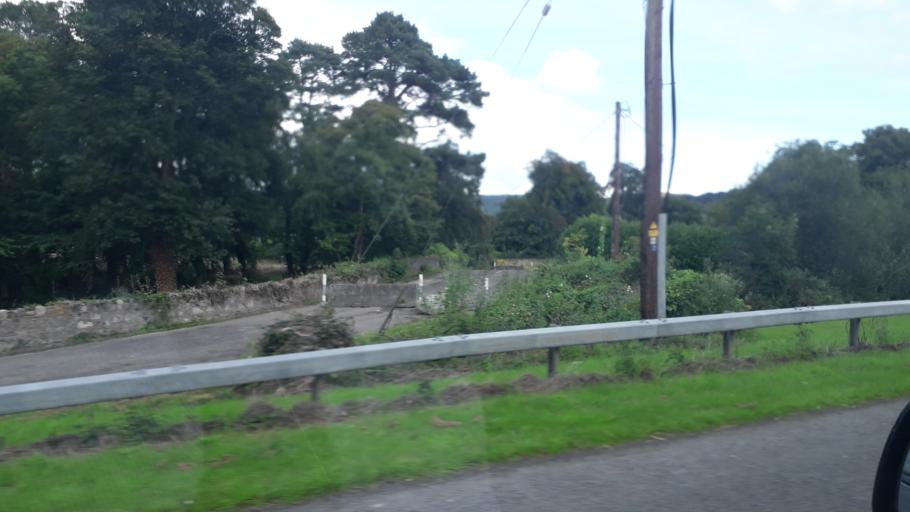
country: IE
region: Leinster
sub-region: Lu
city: Blackrock
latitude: 54.0287
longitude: -6.3514
